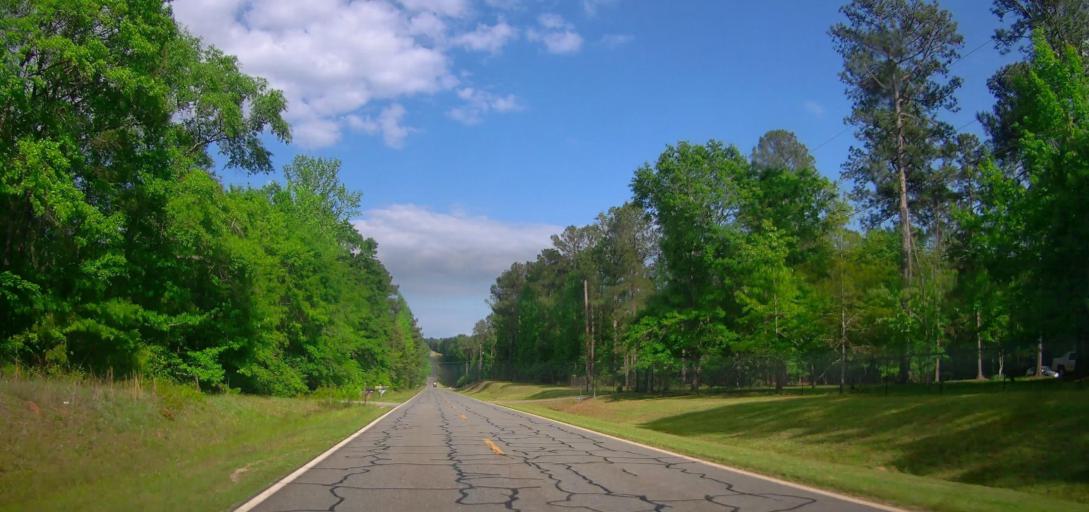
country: US
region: Georgia
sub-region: Baldwin County
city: Hardwick
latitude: 33.0635
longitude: -83.1639
